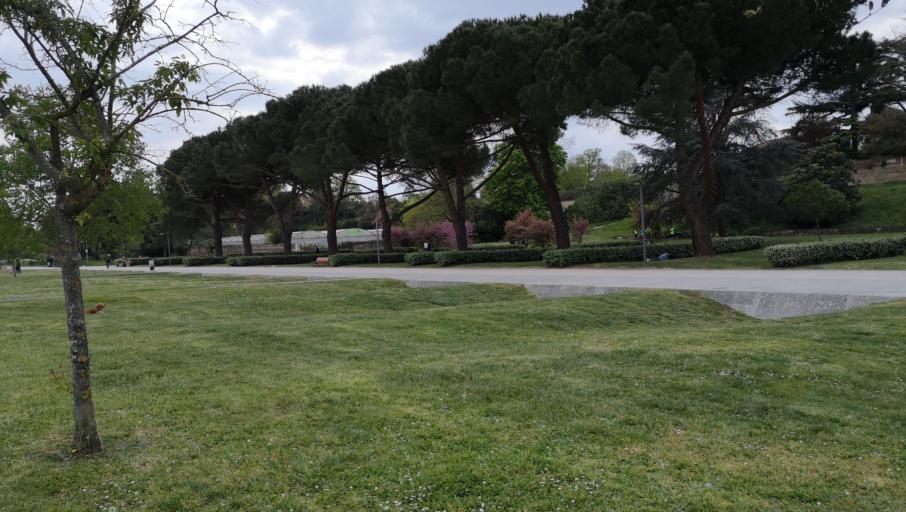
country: FR
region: Midi-Pyrenees
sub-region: Departement de la Haute-Garonne
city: Blagnac
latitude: 43.6330
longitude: 1.4010
